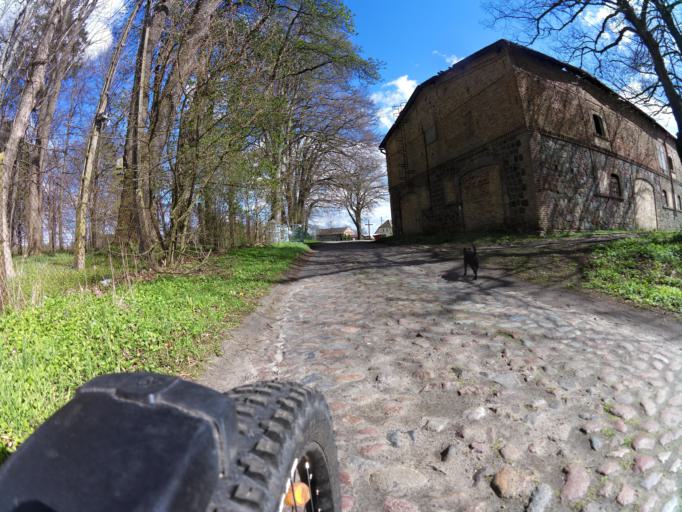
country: PL
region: West Pomeranian Voivodeship
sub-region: Powiat gryficki
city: Gryfice
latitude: 53.8388
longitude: 15.1919
